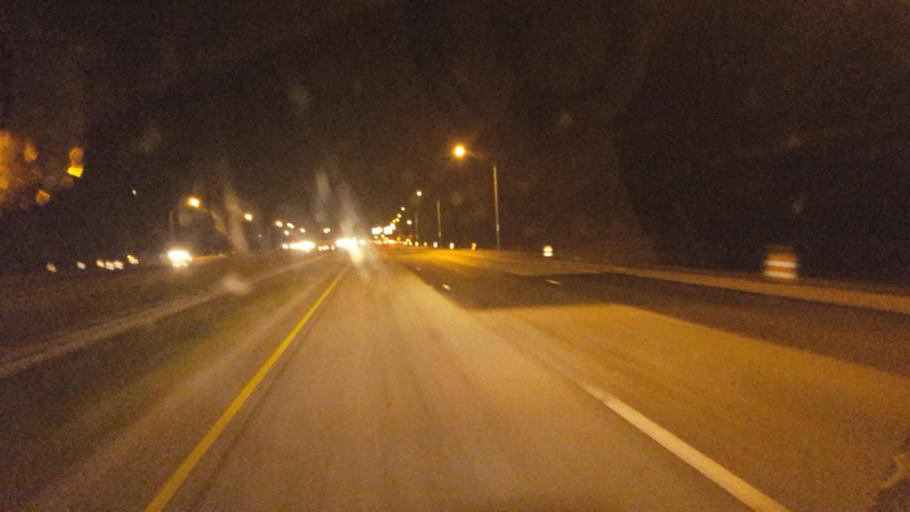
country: US
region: Indiana
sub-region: Hendricks County
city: Plainfield
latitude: 39.6720
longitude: -86.3607
